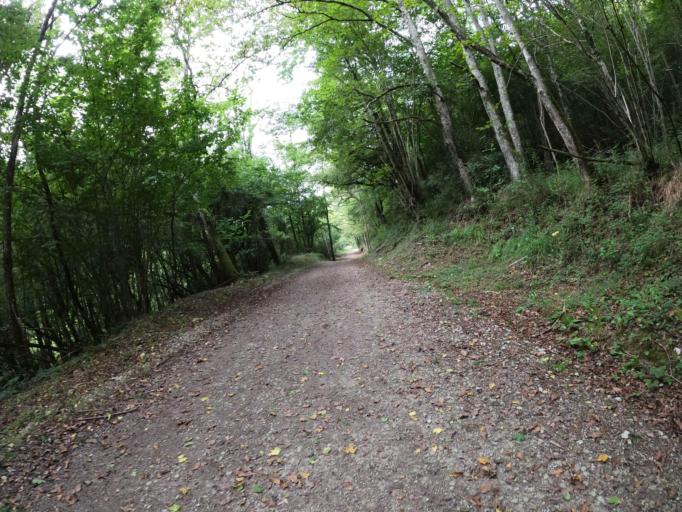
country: ES
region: Navarre
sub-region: Provincia de Navarra
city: Lekunberri
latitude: 42.9855
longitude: -1.8737
